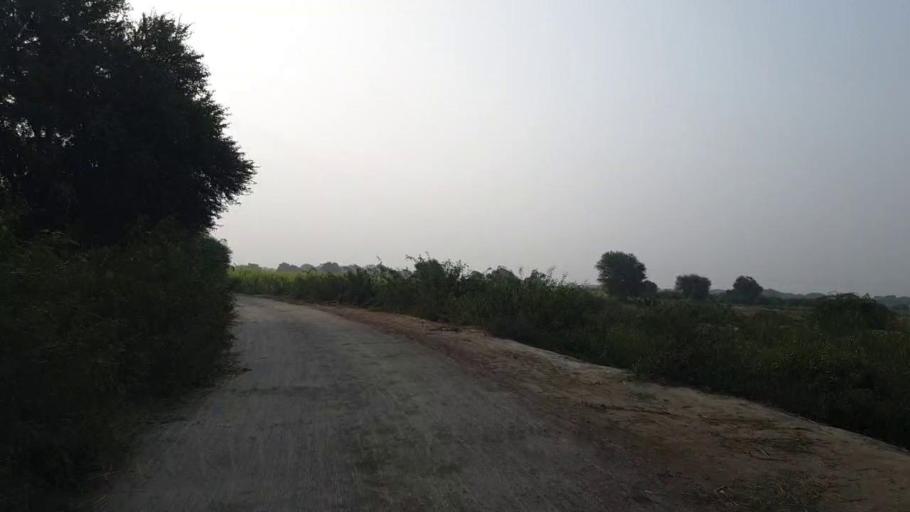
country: PK
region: Sindh
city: Tando Muhammad Khan
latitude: 25.1702
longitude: 68.6071
